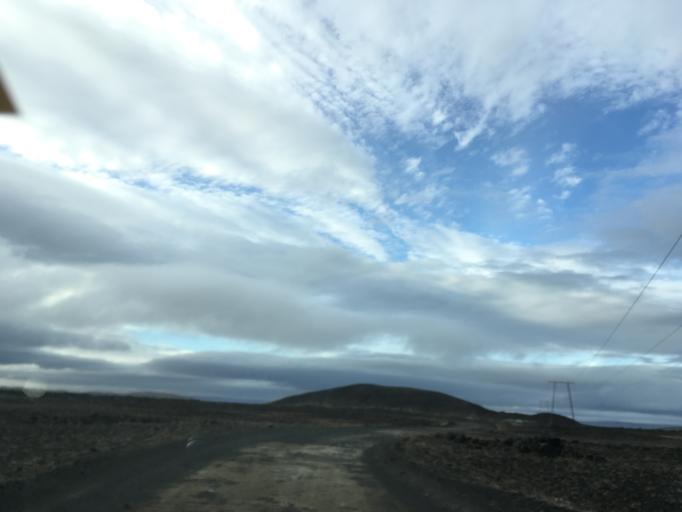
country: IS
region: South
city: Vestmannaeyjar
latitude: 64.1208
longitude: -19.1170
